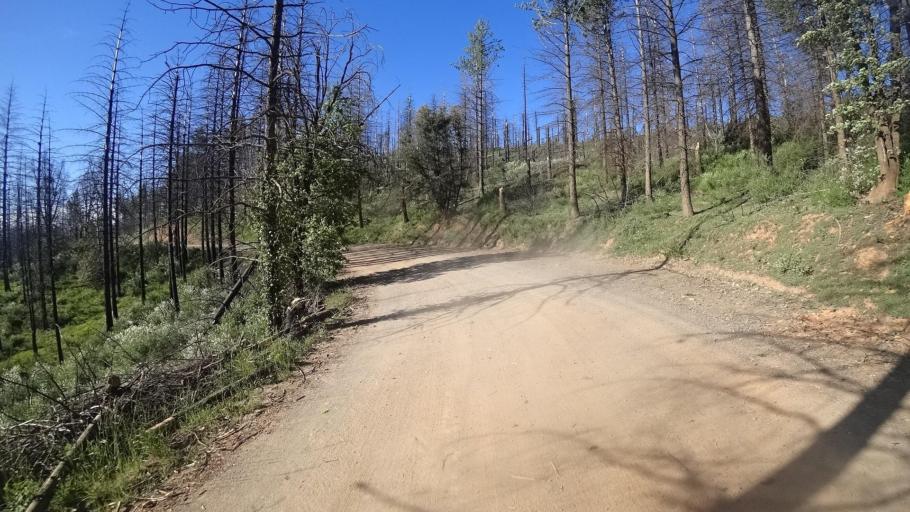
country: US
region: California
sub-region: Lake County
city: Upper Lake
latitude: 39.3417
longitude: -122.9602
